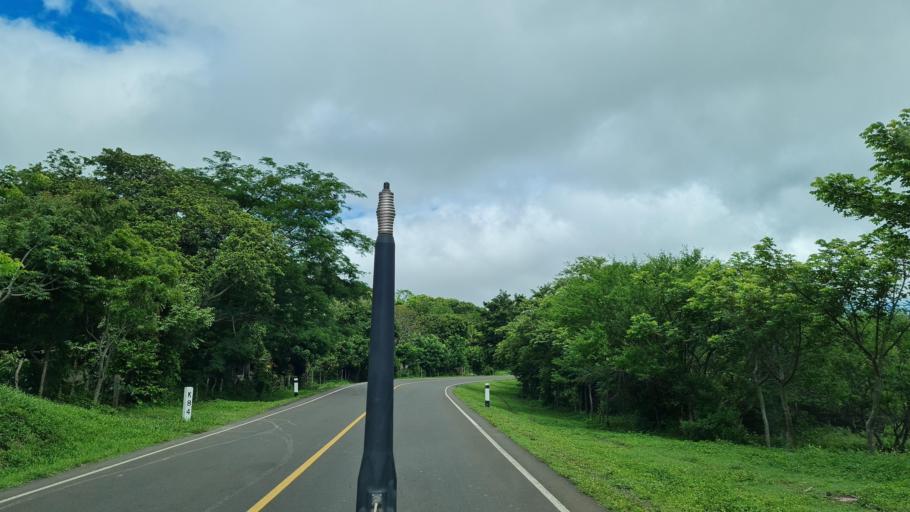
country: NI
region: Matagalpa
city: Terrabona
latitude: 12.5918
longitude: -85.9482
